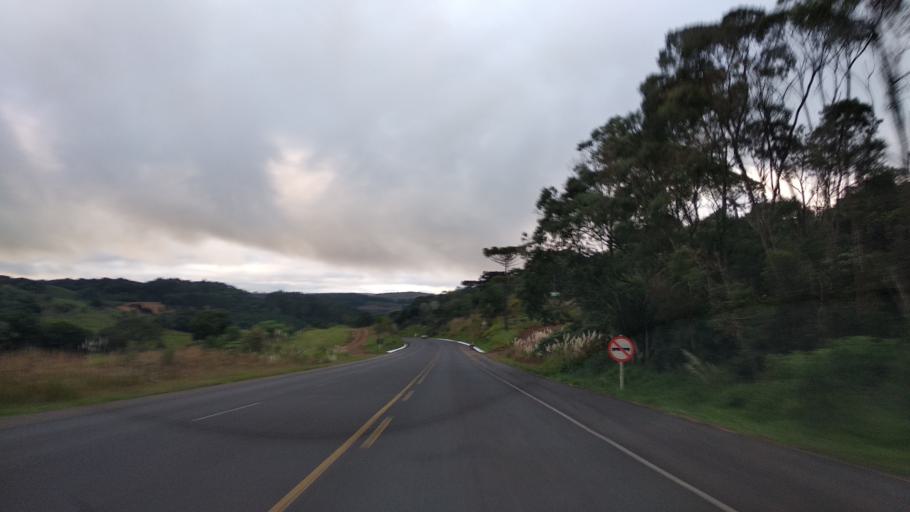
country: BR
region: Santa Catarina
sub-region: Campos Novos
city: Campos Novos
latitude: -27.4453
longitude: -51.0036
